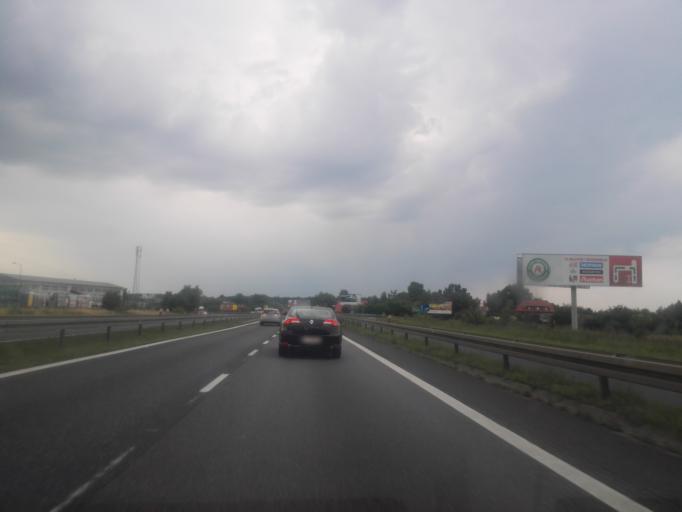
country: PL
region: Silesian Voivodeship
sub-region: Powiat czestochowski
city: Huta Stara B
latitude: 50.7317
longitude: 19.1619
